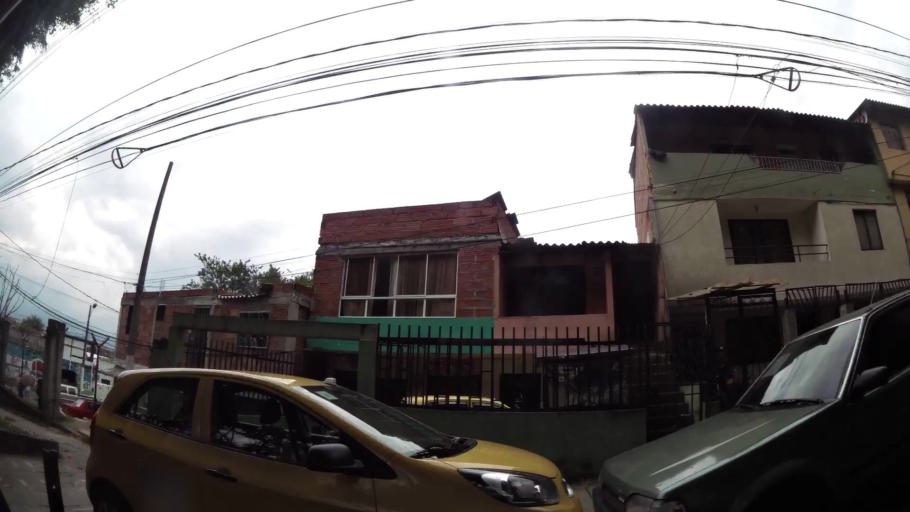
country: CO
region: Antioquia
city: Medellin
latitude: 6.2690
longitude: -75.5986
